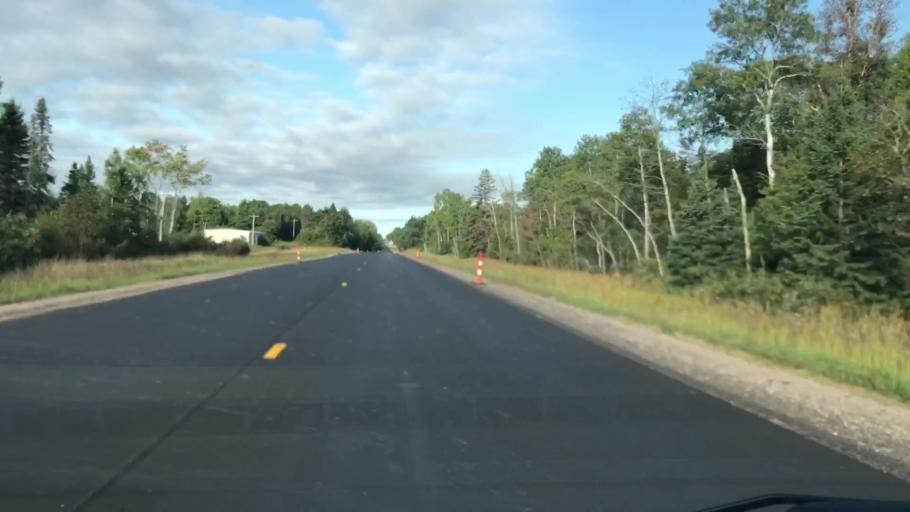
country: US
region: Michigan
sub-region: Mackinac County
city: Saint Ignace
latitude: 46.3460
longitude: -84.9505
